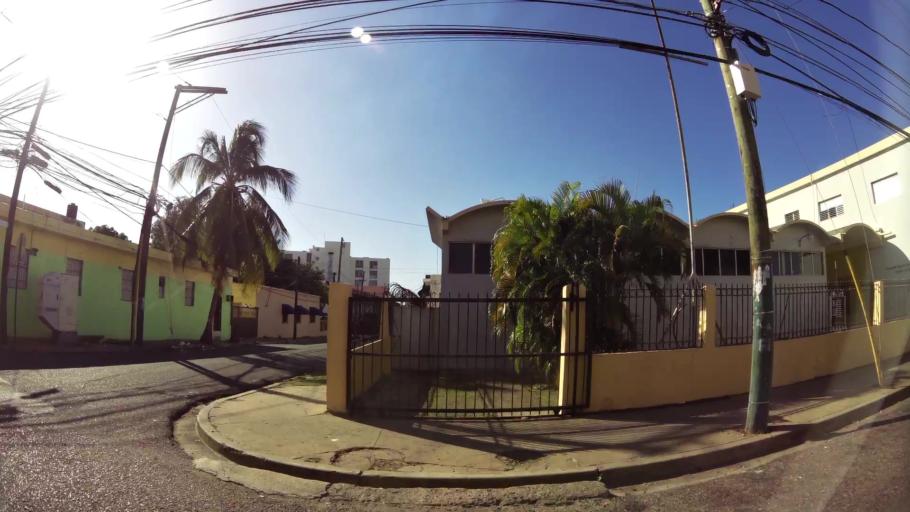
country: DO
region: Nacional
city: Ciudad Nueva
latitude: 18.4675
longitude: -69.8924
